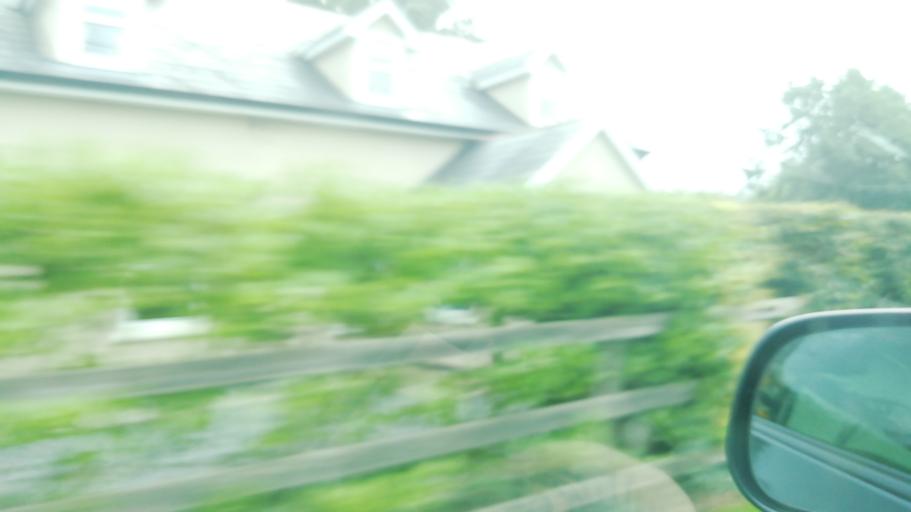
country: IE
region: Munster
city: Fethard
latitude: 52.5224
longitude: -7.6828
